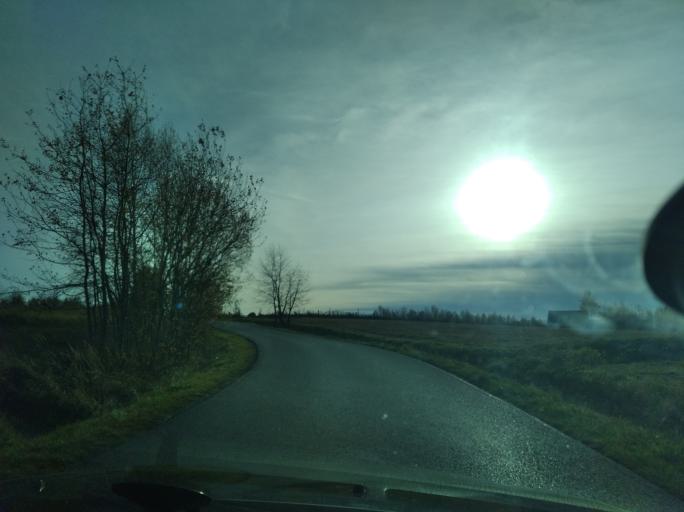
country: PL
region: Subcarpathian Voivodeship
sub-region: Powiat rzeszowski
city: Siedliska
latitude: 49.9347
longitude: 21.9740
